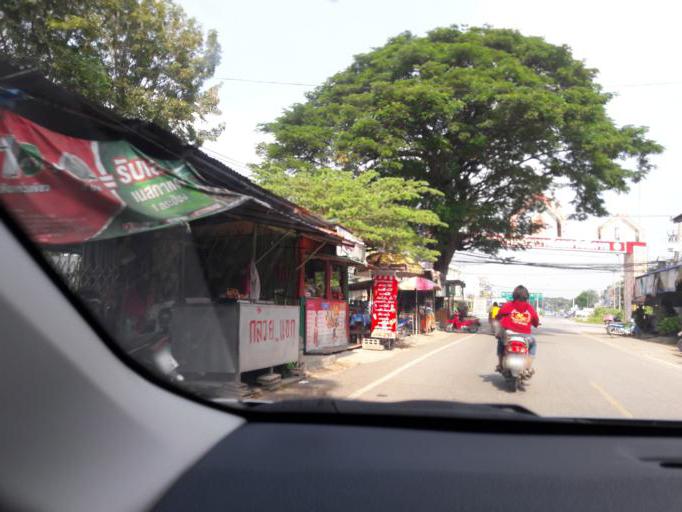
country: TH
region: Ang Thong
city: Ang Thong
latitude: 14.5898
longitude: 100.4462
